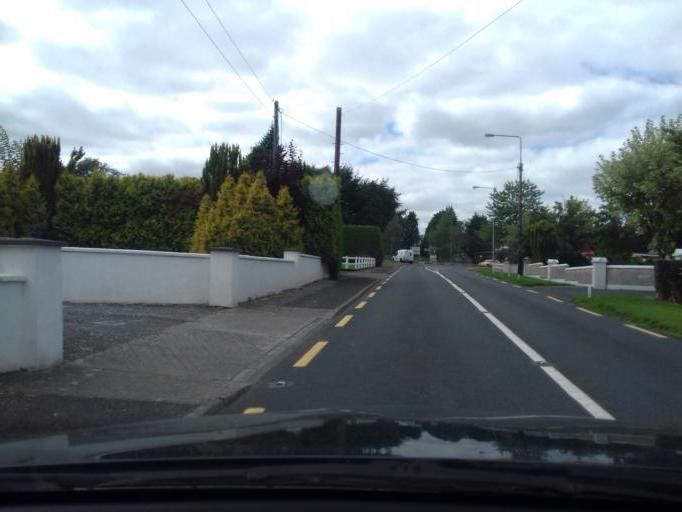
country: IE
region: Leinster
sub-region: Wicklow
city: Baltinglass
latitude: 52.8861
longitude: -6.7037
